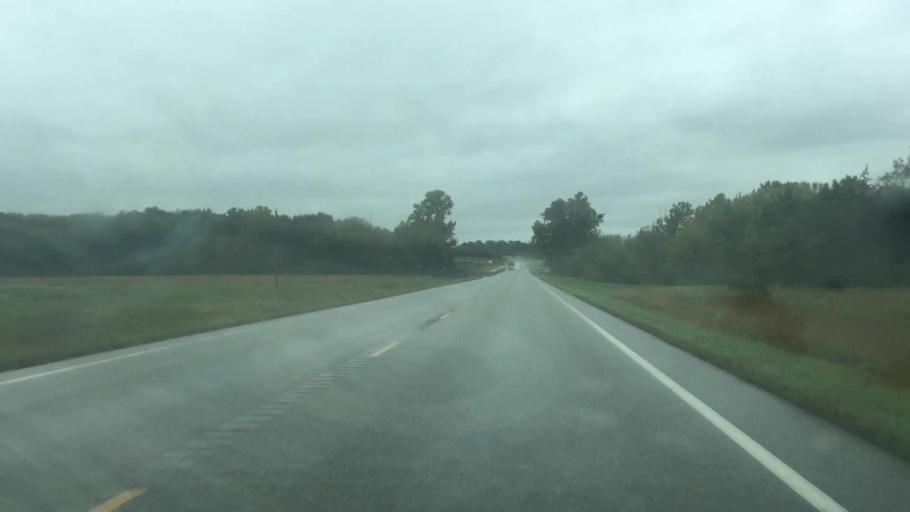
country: US
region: Kansas
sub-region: Anderson County
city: Garnett
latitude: 38.3722
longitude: -95.1159
